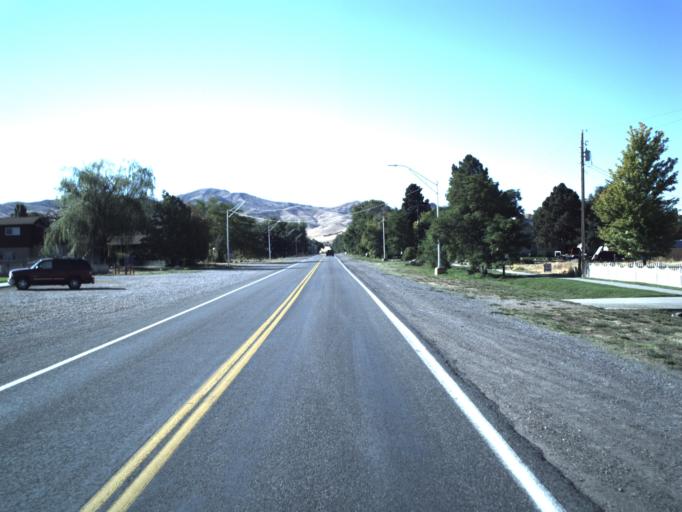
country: US
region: Utah
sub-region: Millard County
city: Delta
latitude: 39.3810
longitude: -112.3361
